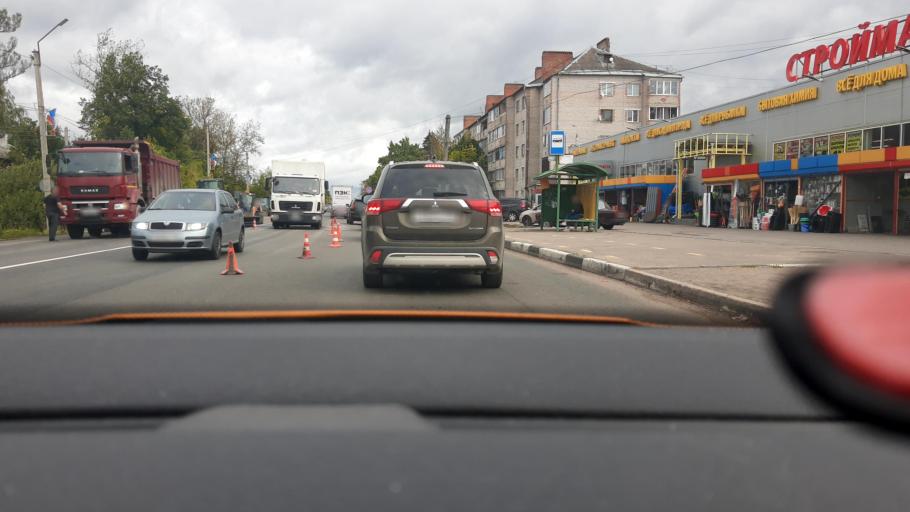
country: RU
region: Moskovskaya
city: Kostino
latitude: 56.0450
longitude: 37.9803
